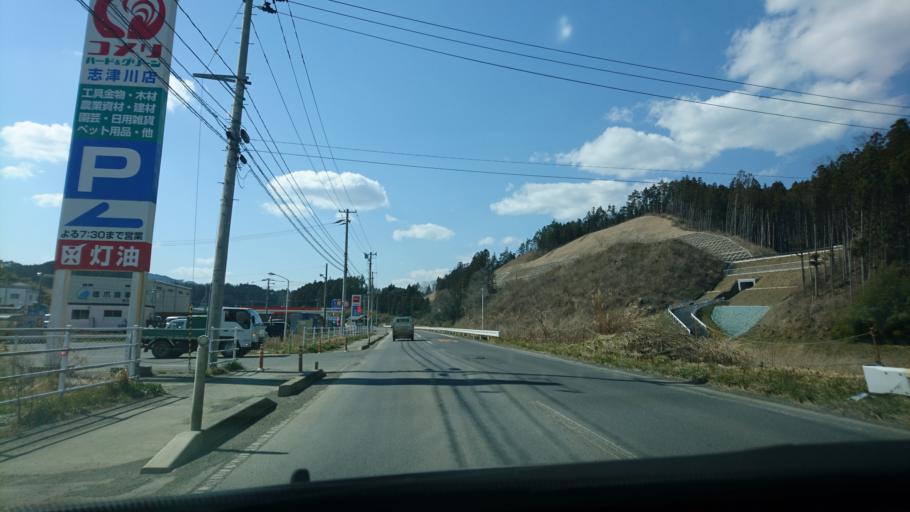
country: JP
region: Miyagi
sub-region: Oshika Gun
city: Onagawa Cho
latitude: 38.6876
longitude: 141.4398
